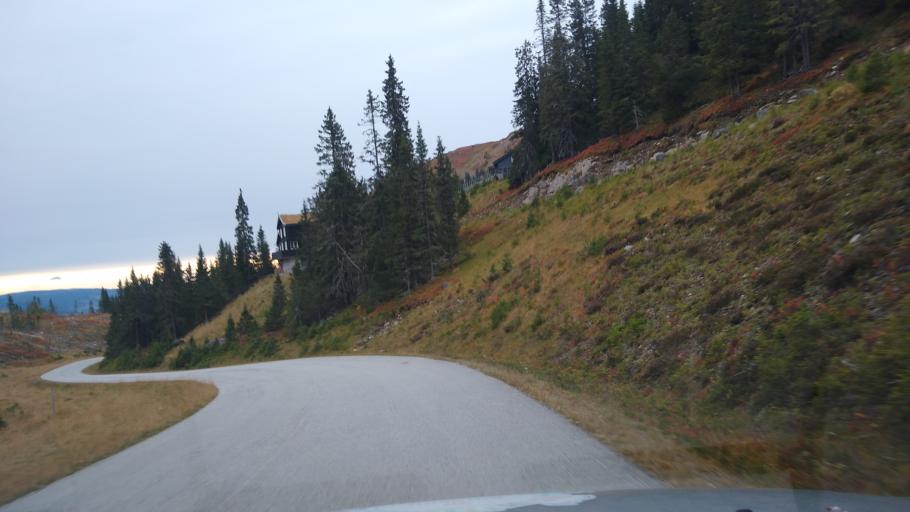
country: NO
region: Oppland
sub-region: Ringebu
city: Ringebu
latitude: 61.4772
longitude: 10.1262
